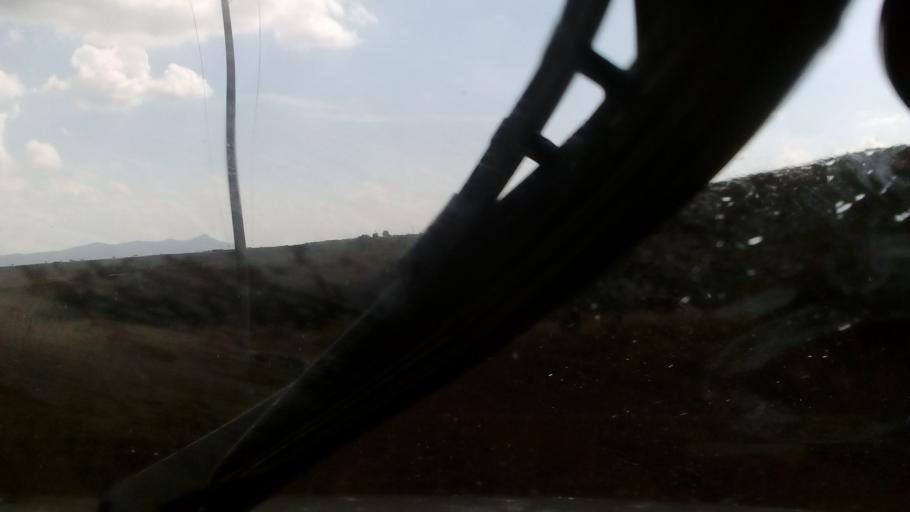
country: MX
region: Guanajuato
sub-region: Silao de la Victoria
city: San Francisco (Banos de Agua Caliente)
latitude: 21.1521
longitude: -101.4353
